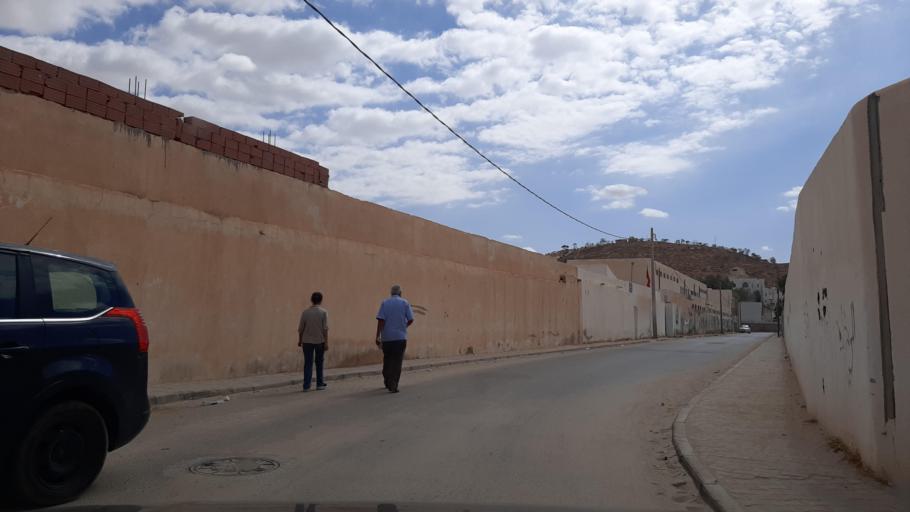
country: TN
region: Tataouine
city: Tataouine
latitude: 32.9286
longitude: 10.4432
